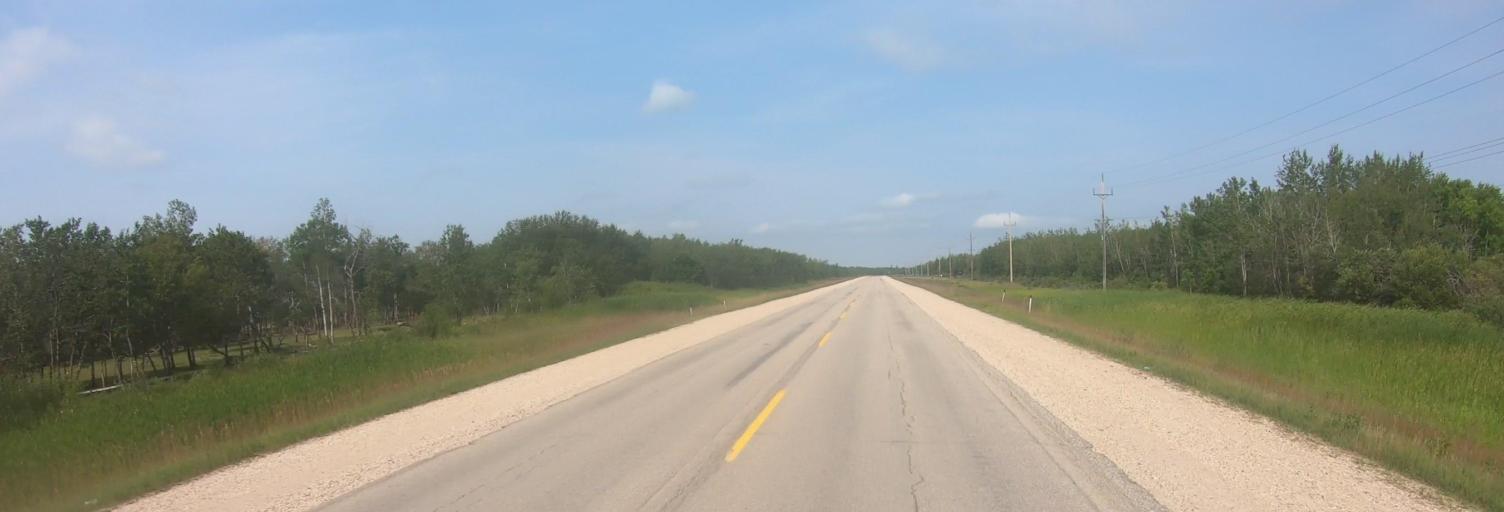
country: CA
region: Manitoba
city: Steinbach
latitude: 49.3532
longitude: -96.6564
